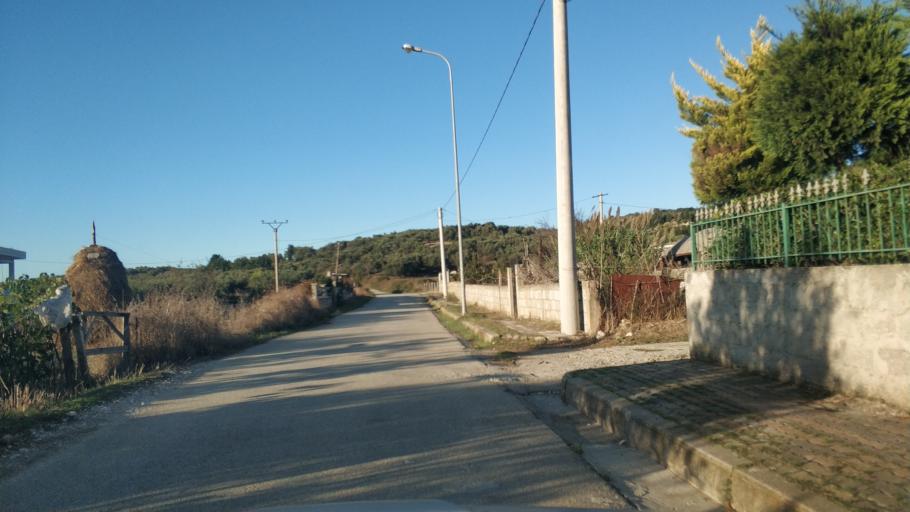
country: AL
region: Vlore
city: Vlore
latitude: 40.5105
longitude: 19.4102
